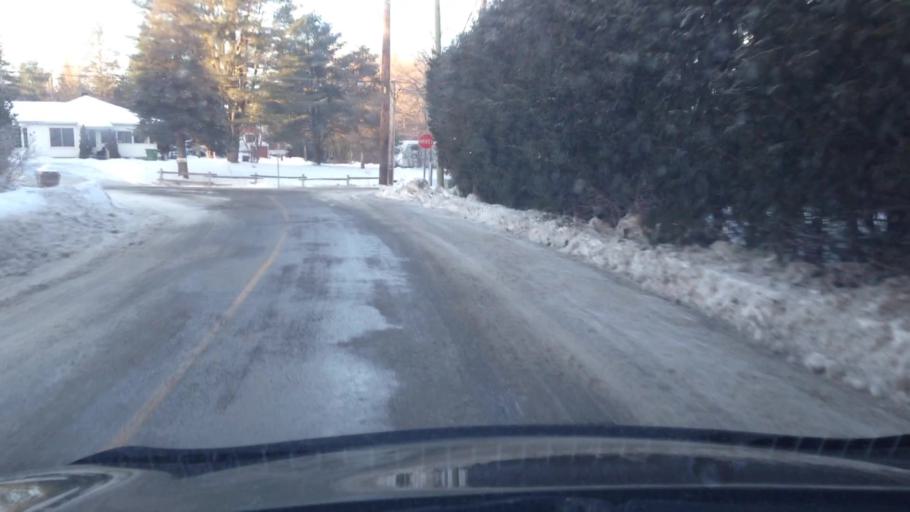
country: CA
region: Quebec
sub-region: Lanaudiere
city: Sainte-Julienne
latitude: 45.9510
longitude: -73.7496
